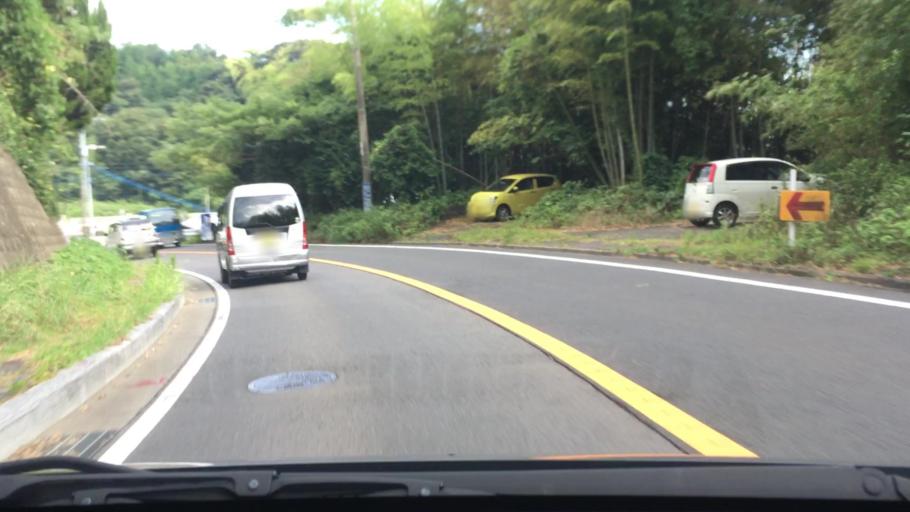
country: JP
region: Nagasaki
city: Togitsu
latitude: 32.8395
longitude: 129.7141
